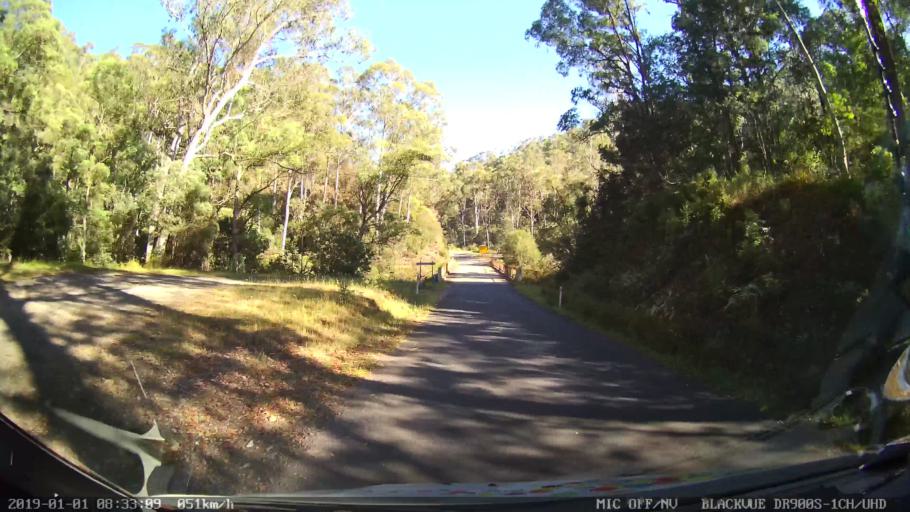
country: AU
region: New South Wales
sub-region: Snowy River
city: Jindabyne
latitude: -36.3570
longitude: 148.2033
